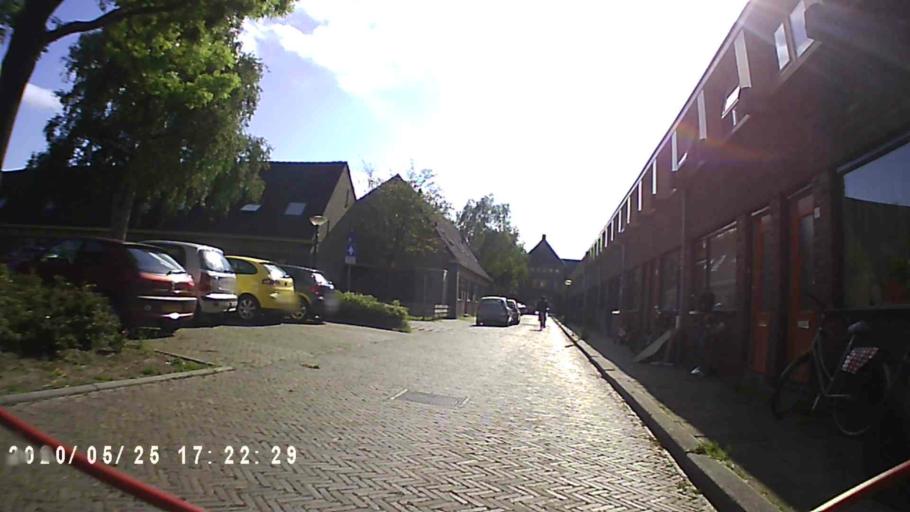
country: NL
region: Groningen
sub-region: Gemeente Groningen
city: Oosterpark
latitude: 53.2254
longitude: 6.5868
